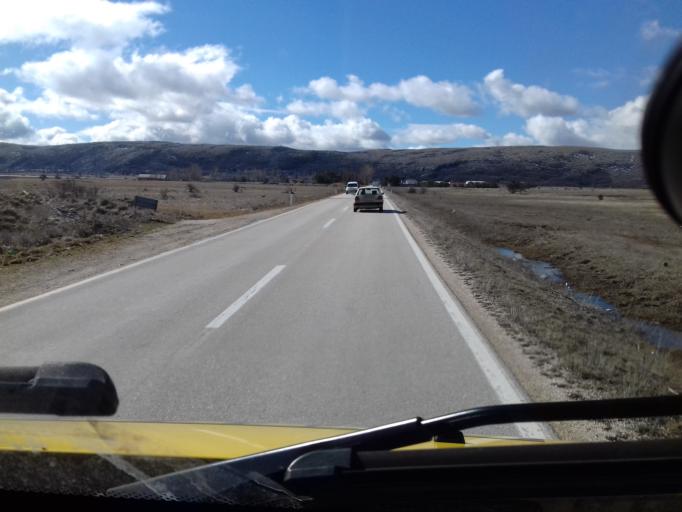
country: BA
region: Federation of Bosnia and Herzegovina
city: Tomislavgrad
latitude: 43.6895
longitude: 17.2084
